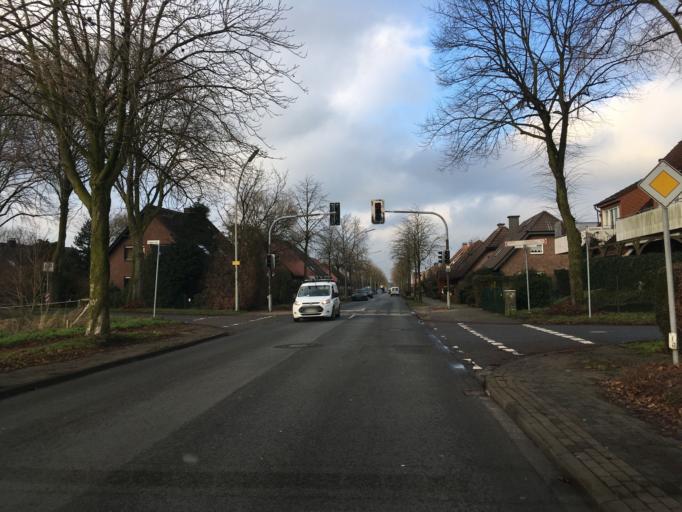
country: DE
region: North Rhine-Westphalia
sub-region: Regierungsbezirk Munster
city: Gescher
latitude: 51.9562
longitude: 6.9926
